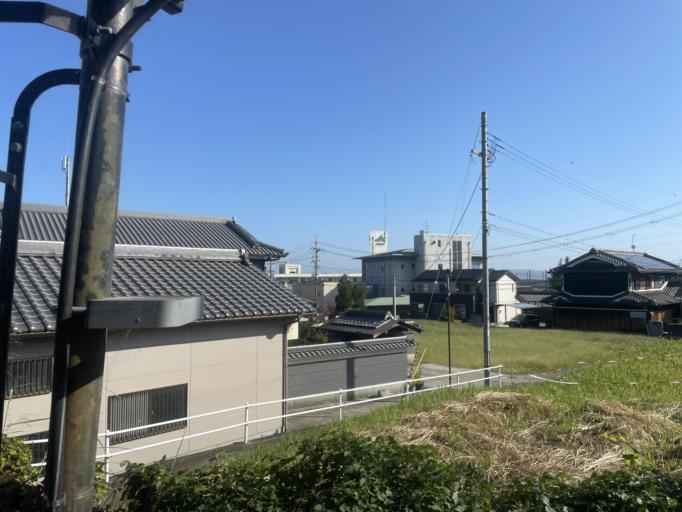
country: JP
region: Osaka
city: Kashihara
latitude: 34.5387
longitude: 135.6869
